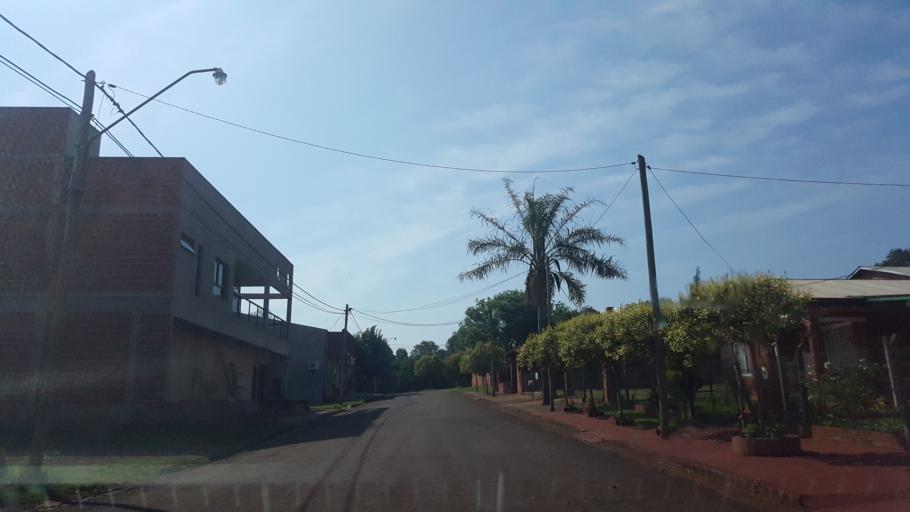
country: AR
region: Misiones
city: Capiovi
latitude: -26.9252
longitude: -55.0586
